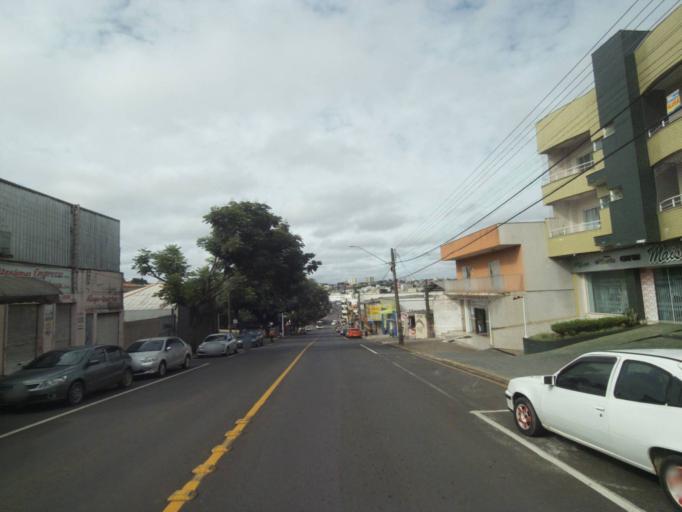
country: BR
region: Parana
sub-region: Telemaco Borba
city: Telemaco Borba
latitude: -24.3211
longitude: -50.6187
